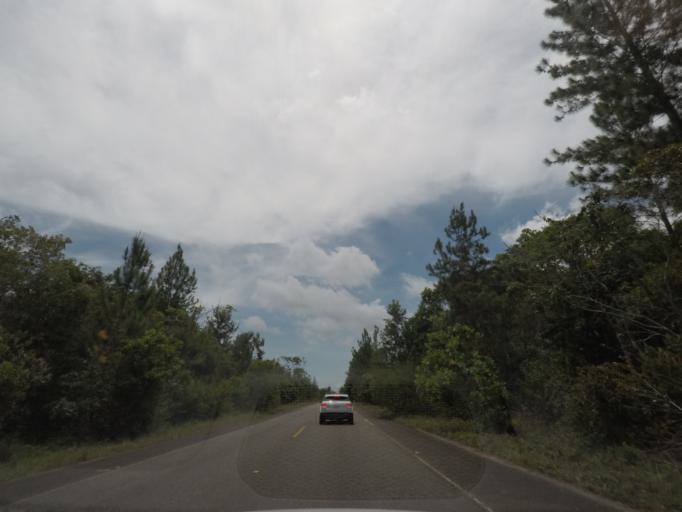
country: BR
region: Bahia
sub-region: Entre Rios
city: Entre Rios
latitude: -12.1473
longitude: -37.7966
